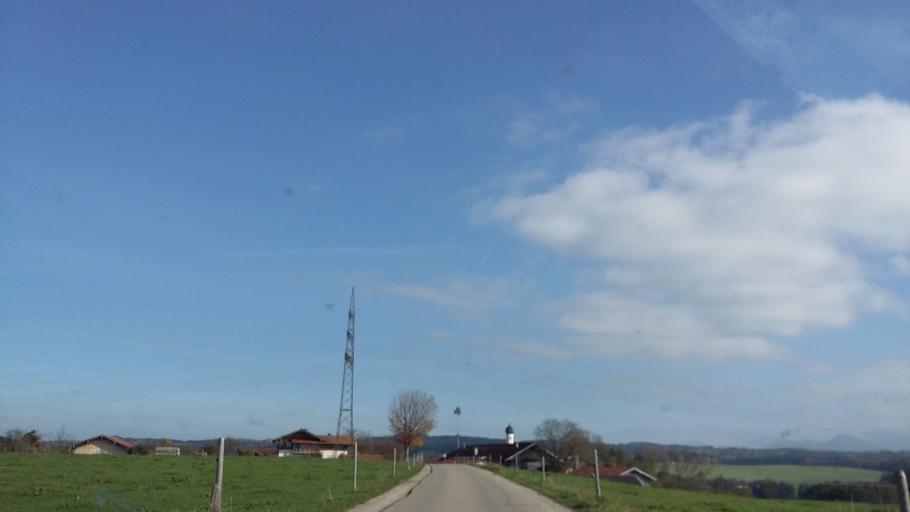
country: DE
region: Bavaria
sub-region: Upper Bavaria
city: Riedering
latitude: 47.8265
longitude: 12.1924
